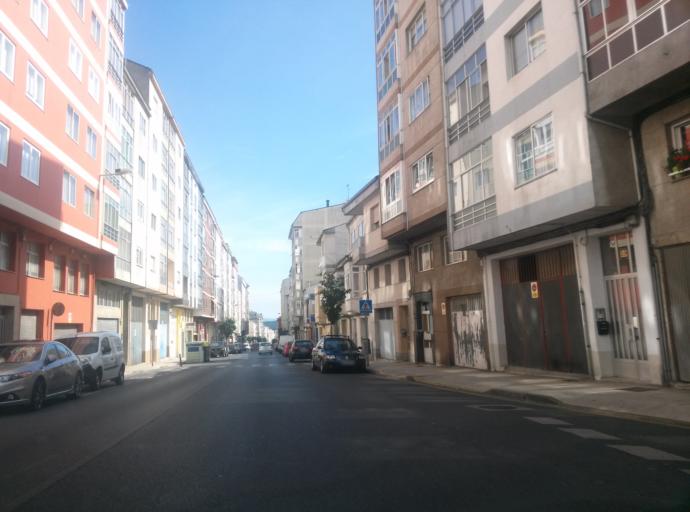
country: ES
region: Galicia
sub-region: Provincia de Lugo
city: Lugo
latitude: 43.0181
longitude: -7.5674
